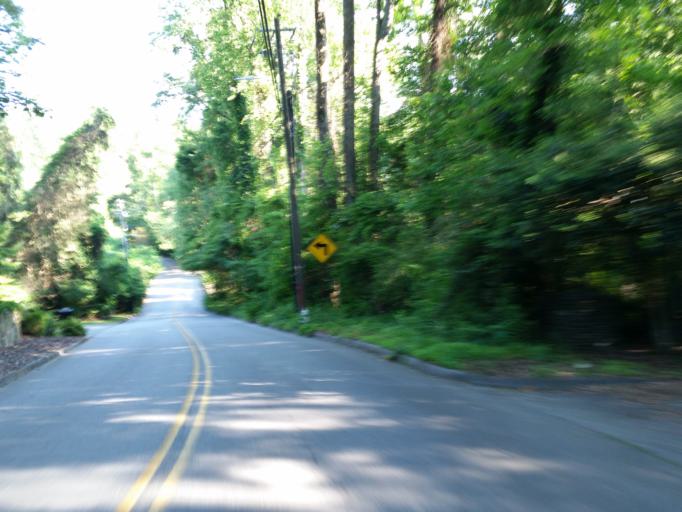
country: US
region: Georgia
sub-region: Cobb County
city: Vinings
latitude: 33.8607
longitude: -84.4249
